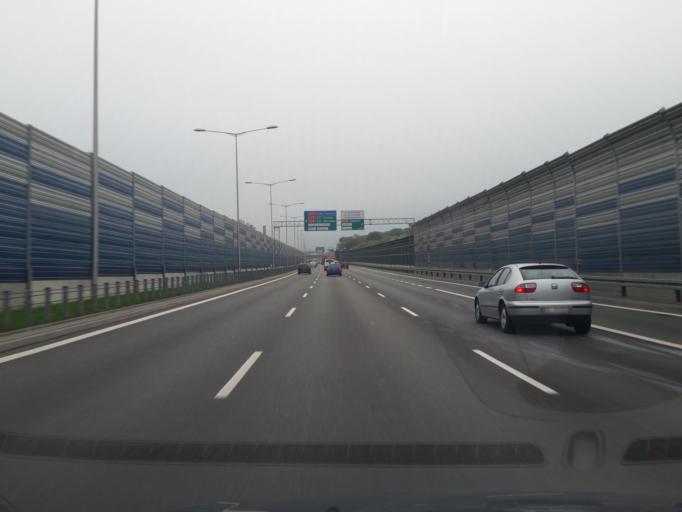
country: PL
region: Masovian Voivodeship
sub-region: Warszawa
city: Zoliborz
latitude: 52.2783
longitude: 20.9763
